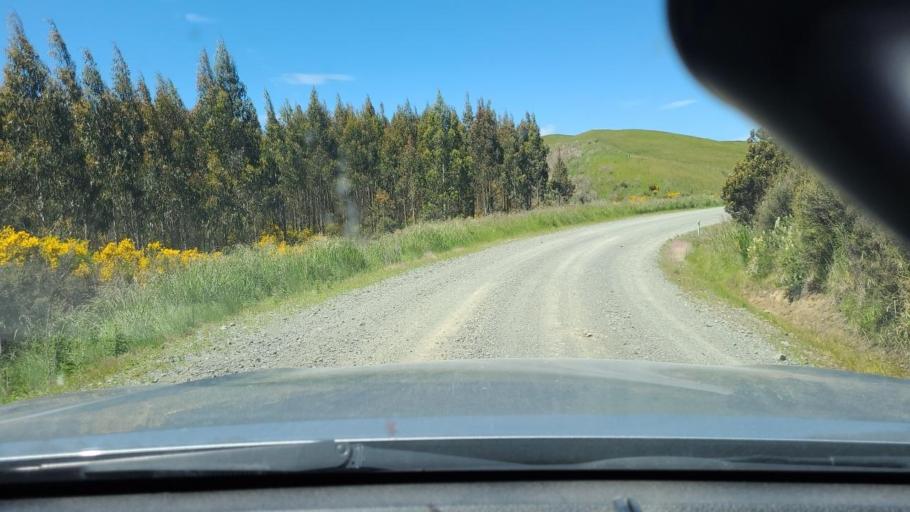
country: NZ
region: Southland
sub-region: Southland District
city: Riverton
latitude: -45.9232
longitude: 167.7965
